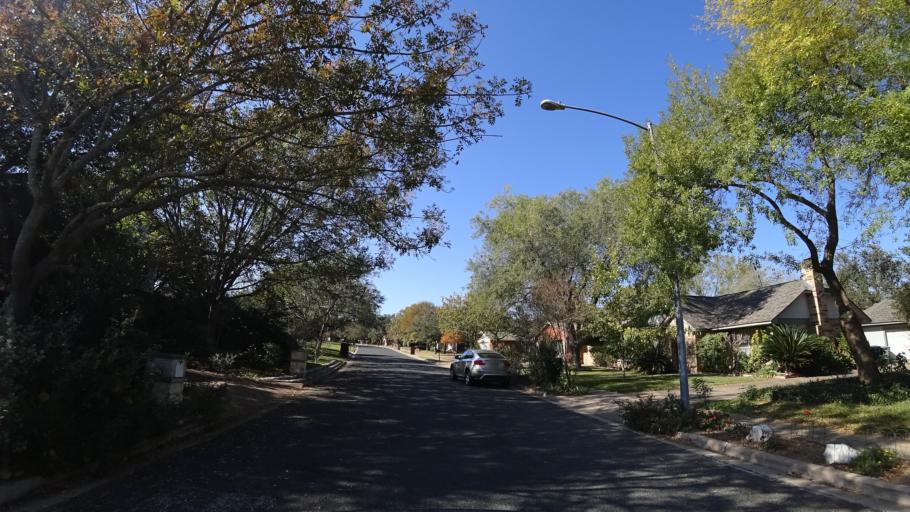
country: US
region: Texas
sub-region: Travis County
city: Shady Hollow
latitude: 30.2237
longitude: -97.8577
